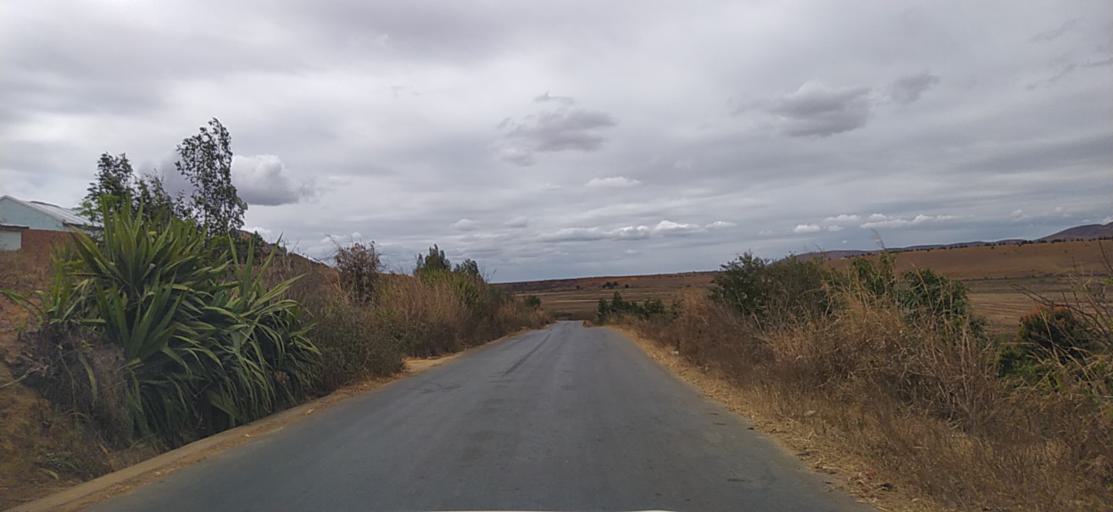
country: MG
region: Alaotra Mangoro
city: Ambatondrazaka
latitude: -17.9274
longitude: 48.2576
